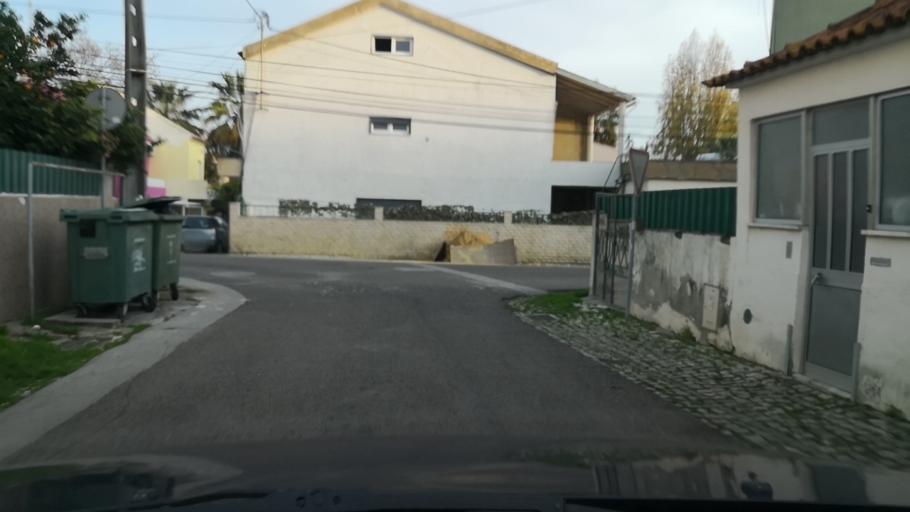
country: PT
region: Setubal
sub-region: Setubal
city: Setubal
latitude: 38.5253
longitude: -8.8633
